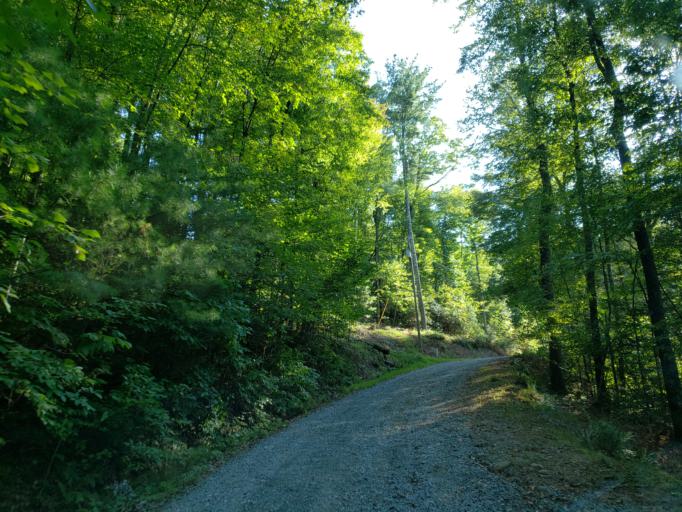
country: US
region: Georgia
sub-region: Fannin County
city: Blue Ridge
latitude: 34.6746
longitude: -84.2629
